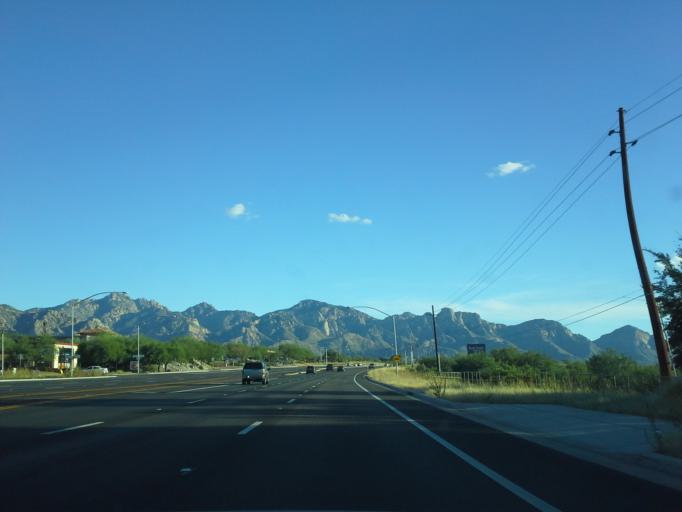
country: US
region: Arizona
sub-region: Pima County
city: Catalina
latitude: 32.4853
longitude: -110.9229
